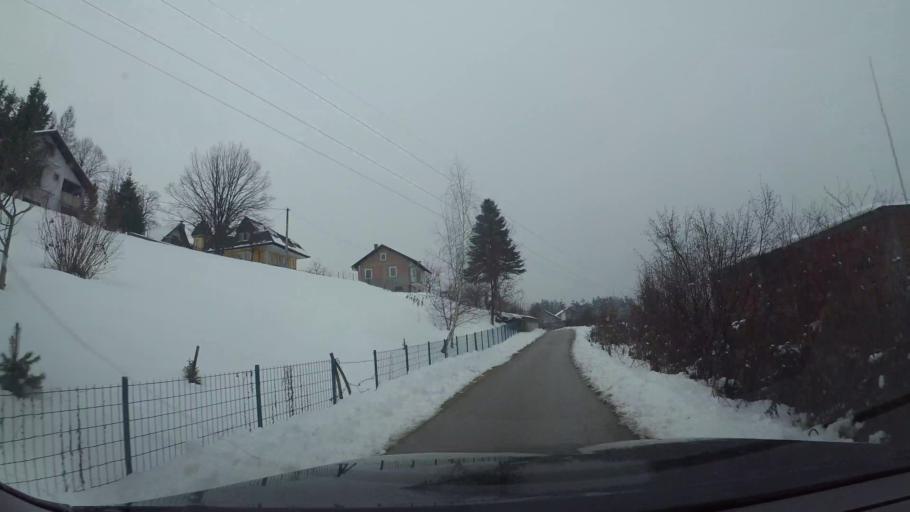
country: BA
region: Federation of Bosnia and Herzegovina
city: Hadzici
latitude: 43.8516
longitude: 18.2670
